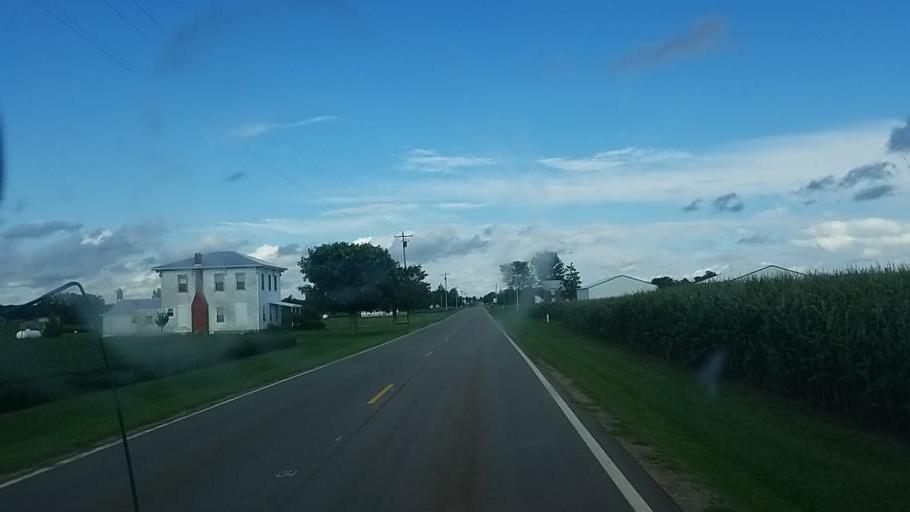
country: US
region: Ohio
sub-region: Wyandot County
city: Upper Sandusky
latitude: 40.8027
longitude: -83.3868
